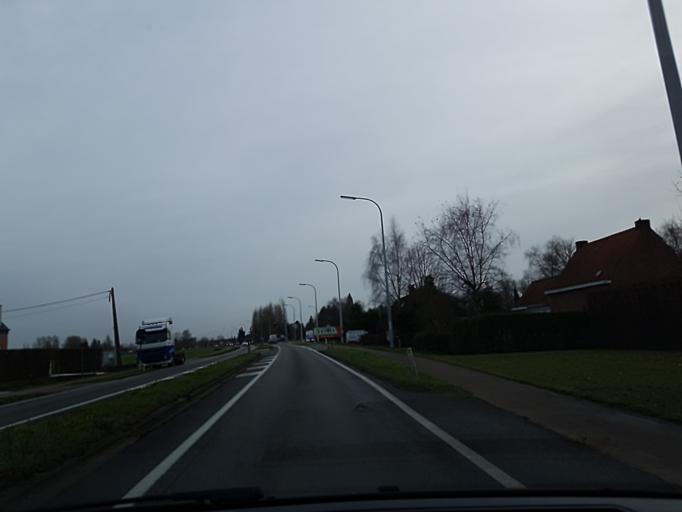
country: BE
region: Flanders
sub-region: Provincie Antwerpen
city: Lier
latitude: 51.1101
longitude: 4.5942
